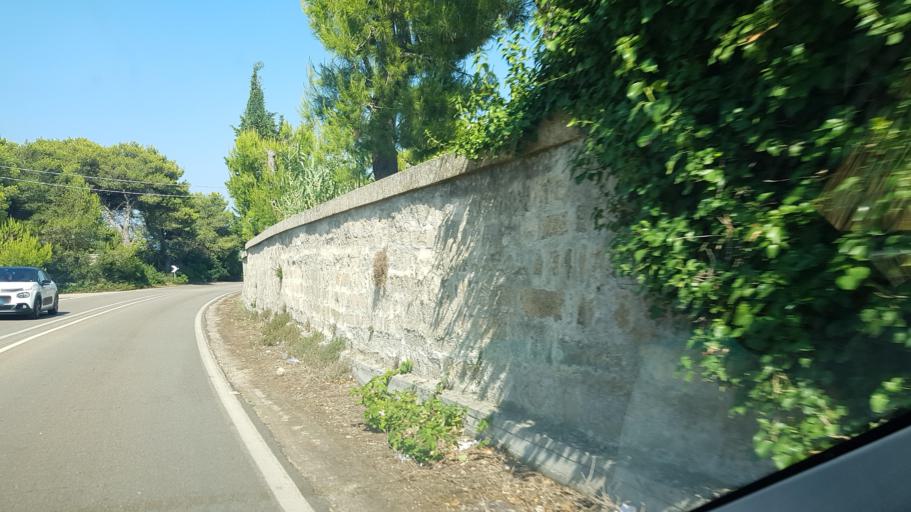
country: IT
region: Apulia
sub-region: Provincia di Lecce
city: Gemini
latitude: 39.8668
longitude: 18.2109
